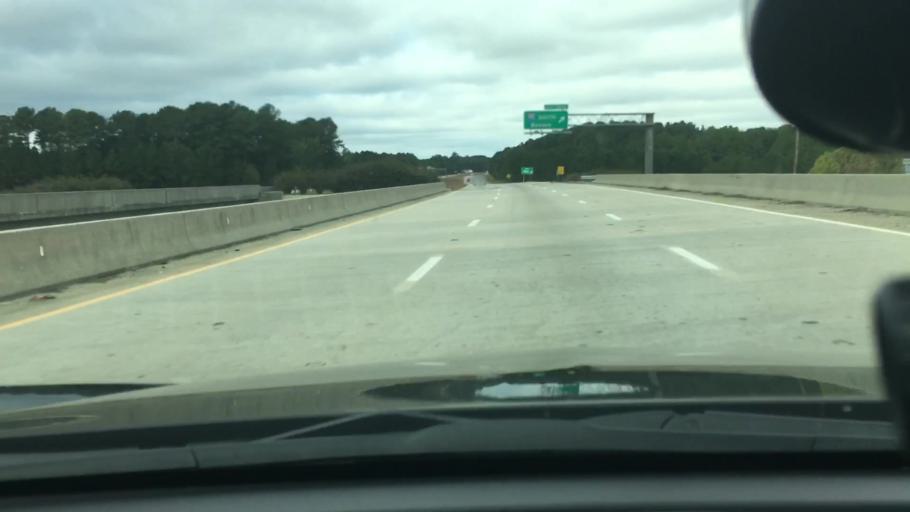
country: US
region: North Carolina
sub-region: Wilson County
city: Lucama
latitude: 35.7348
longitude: -78.0119
